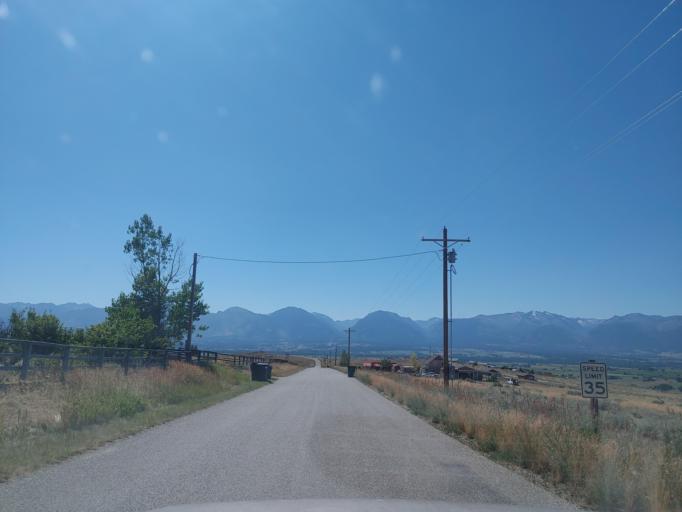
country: US
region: Montana
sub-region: Ravalli County
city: Hamilton
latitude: 46.3490
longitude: -114.0385
